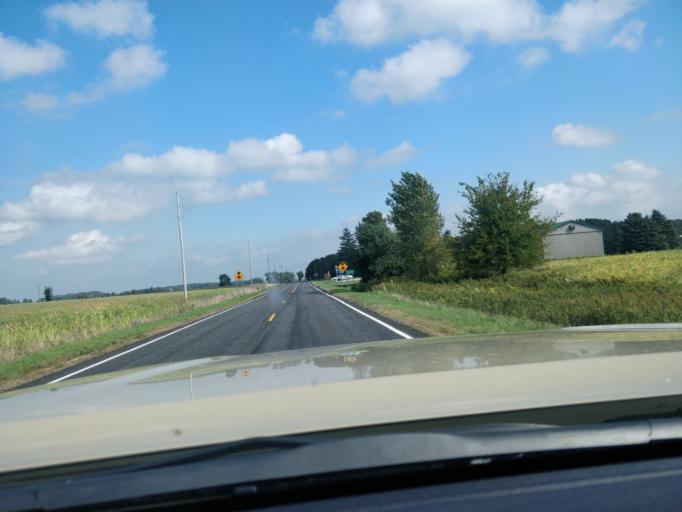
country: US
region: Michigan
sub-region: Ionia County
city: Saranac
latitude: 42.8862
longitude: -85.1371
